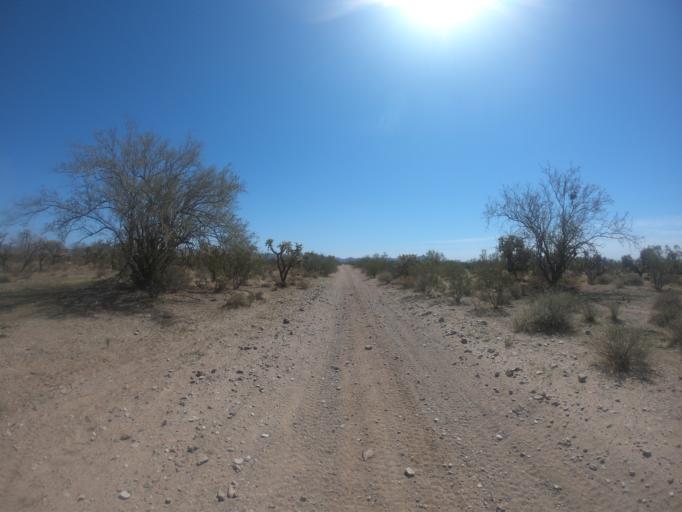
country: US
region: Arizona
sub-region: Pinal County
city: Gold Camp
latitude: 33.2405
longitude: -111.3148
